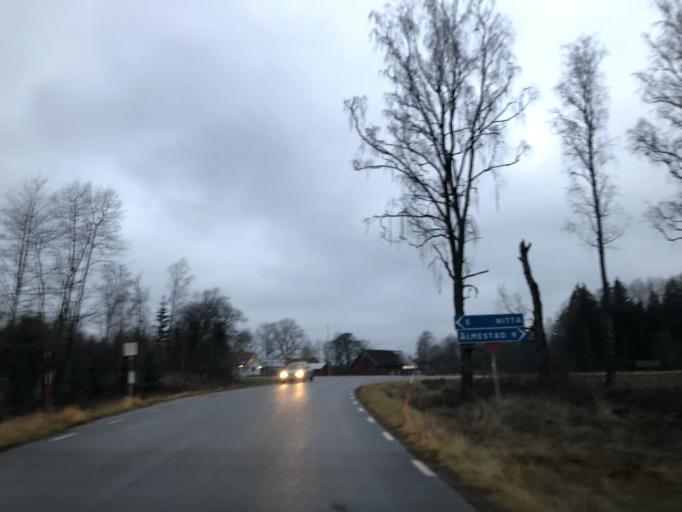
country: SE
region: Vaestra Goetaland
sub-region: Ulricehamns Kommun
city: Ulricehamn
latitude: 57.8521
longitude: 13.2531
